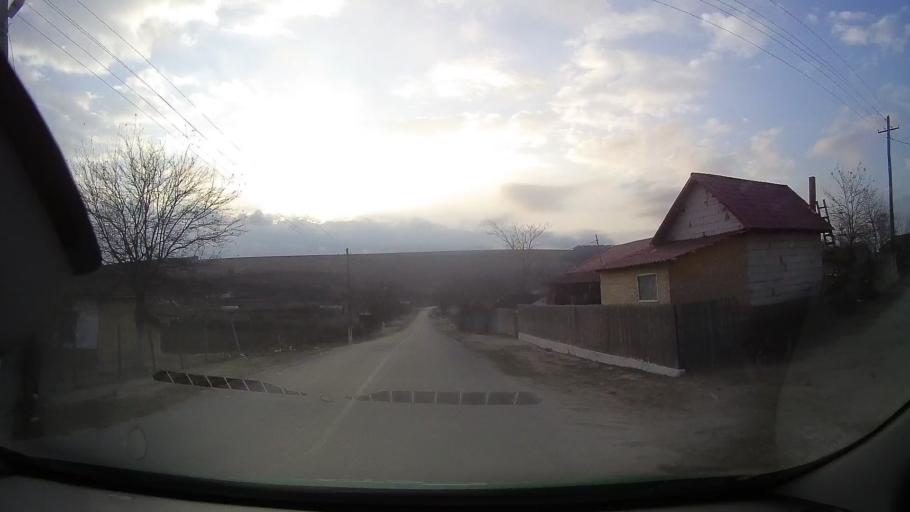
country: RO
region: Constanta
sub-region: Comuna Dobromir
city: Dobromir
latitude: 44.0223
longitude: 27.8750
